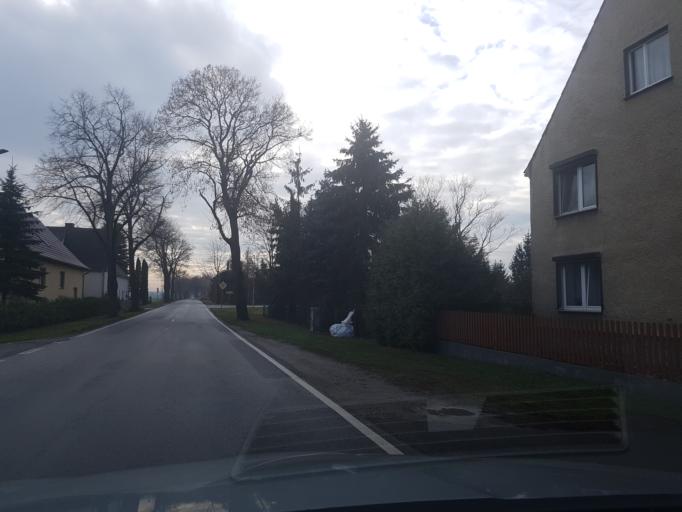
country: DE
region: Brandenburg
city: Plessa
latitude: 51.4325
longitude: 13.6247
